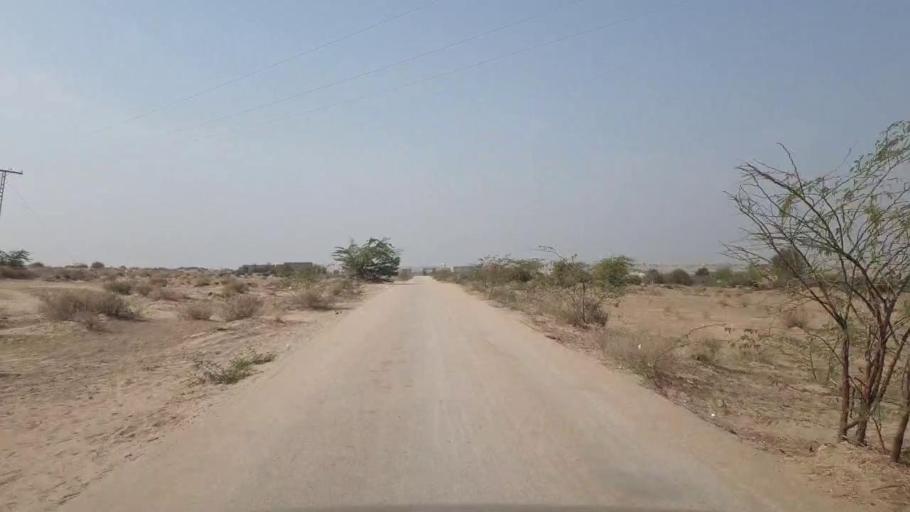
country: PK
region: Sindh
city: Umarkot
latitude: 25.3272
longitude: 69.7331
